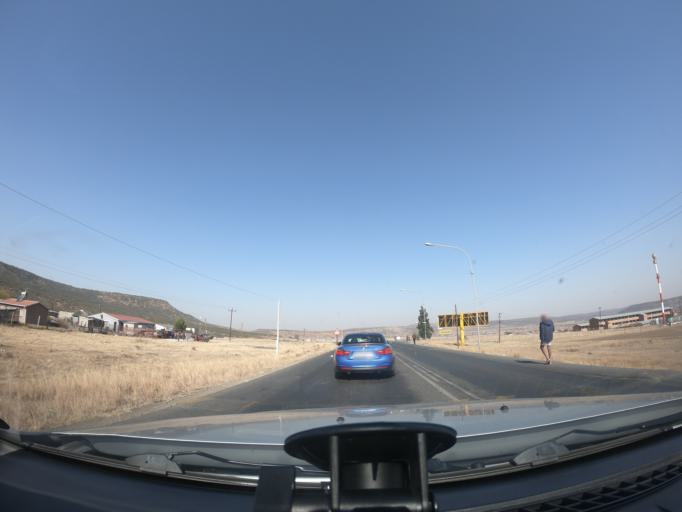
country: ZA
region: KwaZulu-Natal
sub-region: uThukela District Municipality
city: Ladysmith
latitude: -28.5711
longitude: 29.8343
